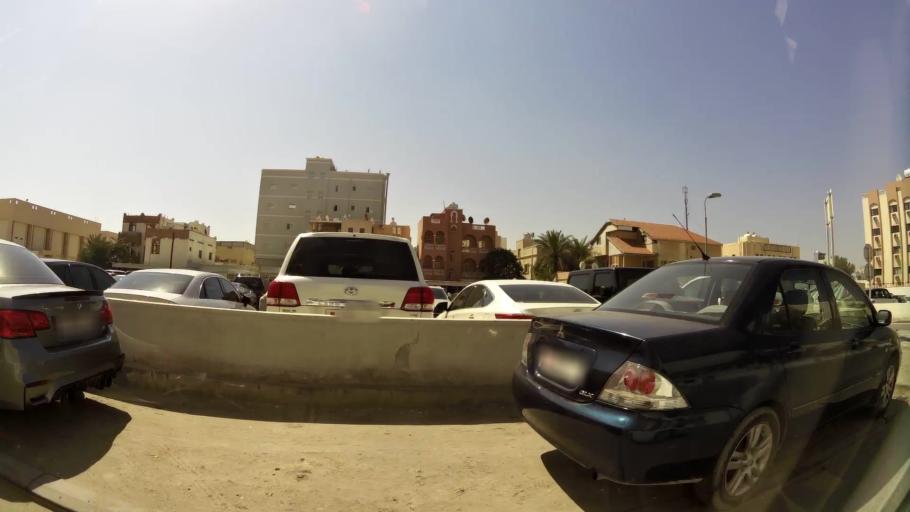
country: BH
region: Manama
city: Manama
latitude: 26.2128
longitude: 50.6026
